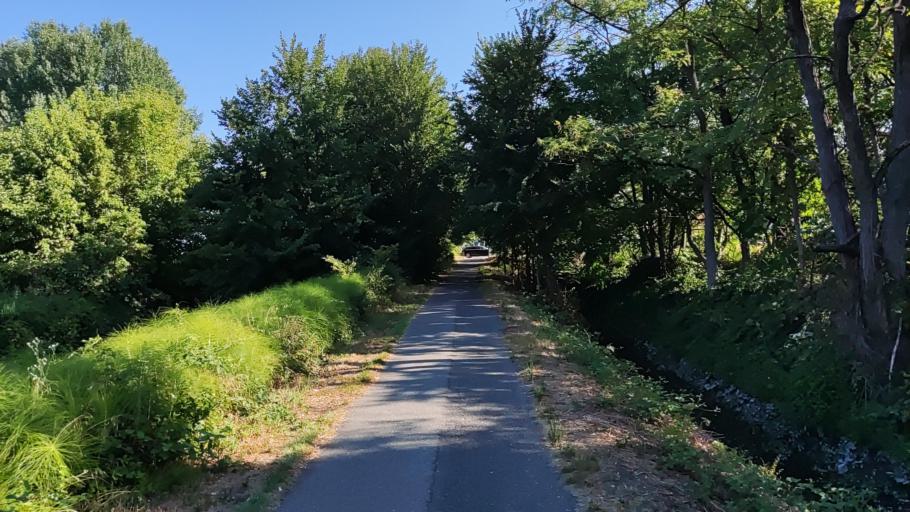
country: IT
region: Lombardy
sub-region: Citta metropolitana di Milano
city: Fizzonasco
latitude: 45.3663
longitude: 9.1893
